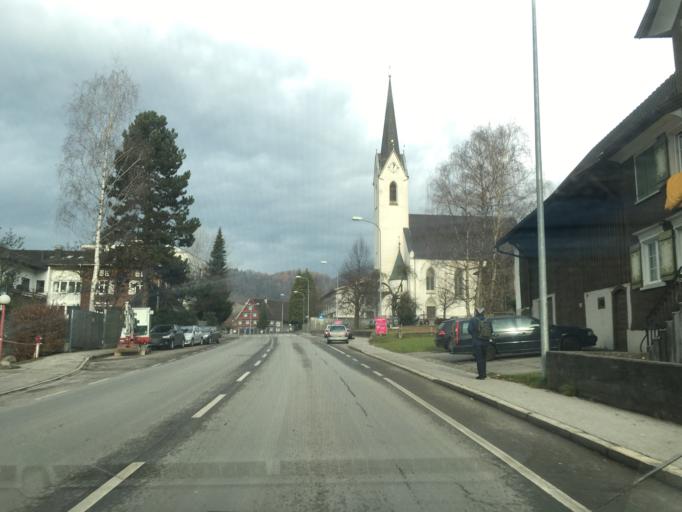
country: AT
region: Vorarlberg
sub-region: Politischer Bezirk Feldkirch
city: Weiler
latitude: 47.3021
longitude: 9.6526
